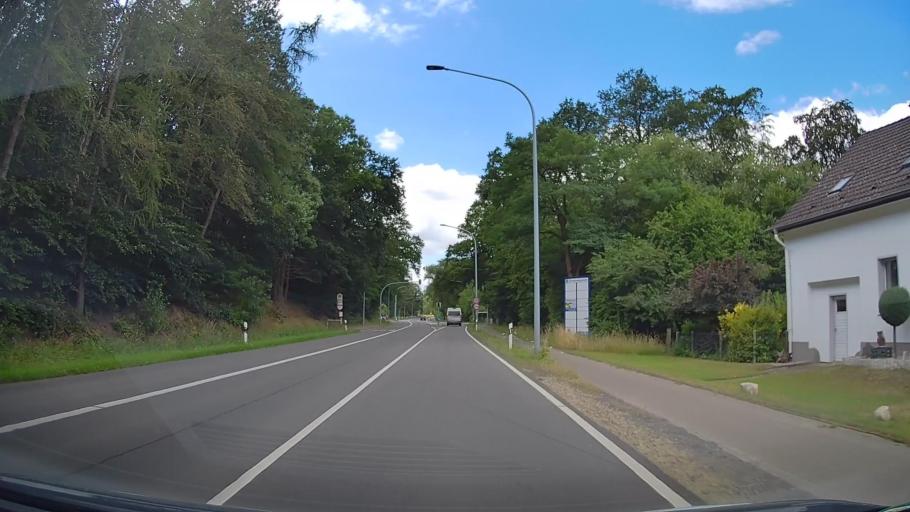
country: DE
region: Lower Saxony
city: Belm
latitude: 52.2941
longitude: 8.1001
